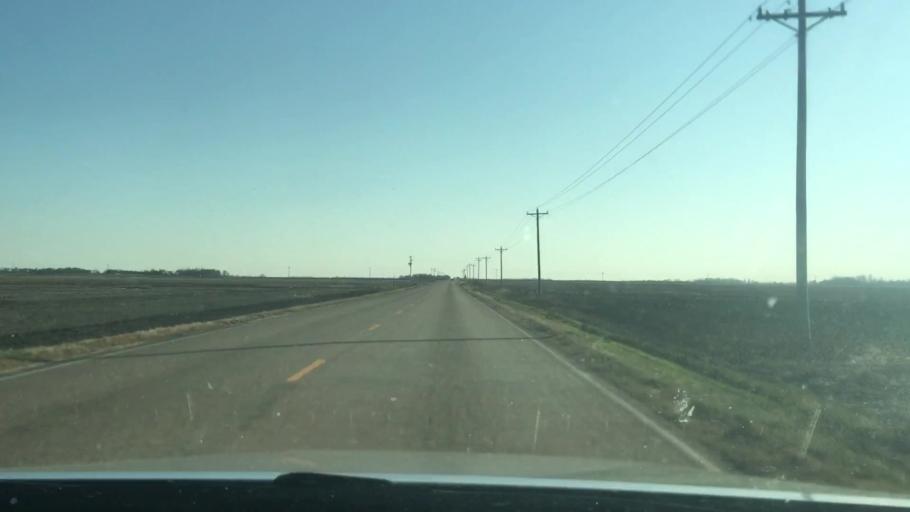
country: US
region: Kansas
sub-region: Reno County
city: Nickerson
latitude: 38.2239
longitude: -98.0877
